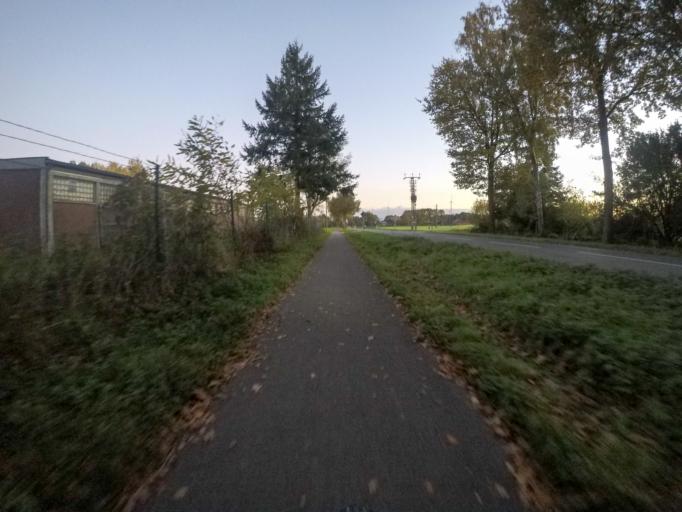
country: DE
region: North Rhine-Westphalia
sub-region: Regierungsbezirk Dusseldorf
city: Bocholt
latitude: 51.8066
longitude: 6.5725
